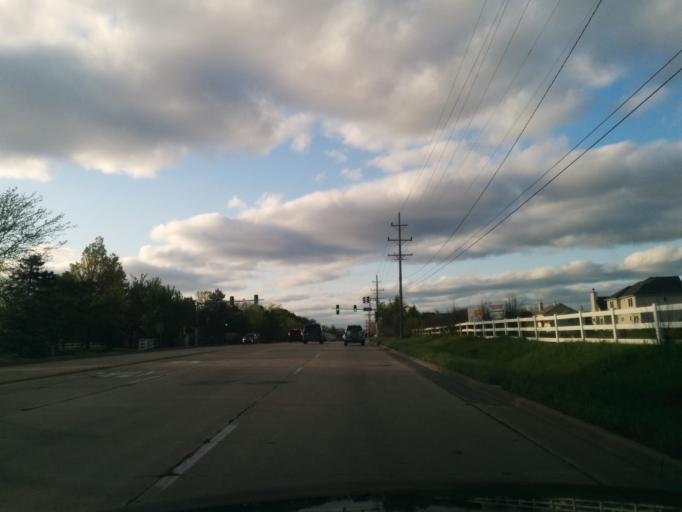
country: US
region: Illinois
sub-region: DuPage County
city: Wayne
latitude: 41.9562
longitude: -88.2054
